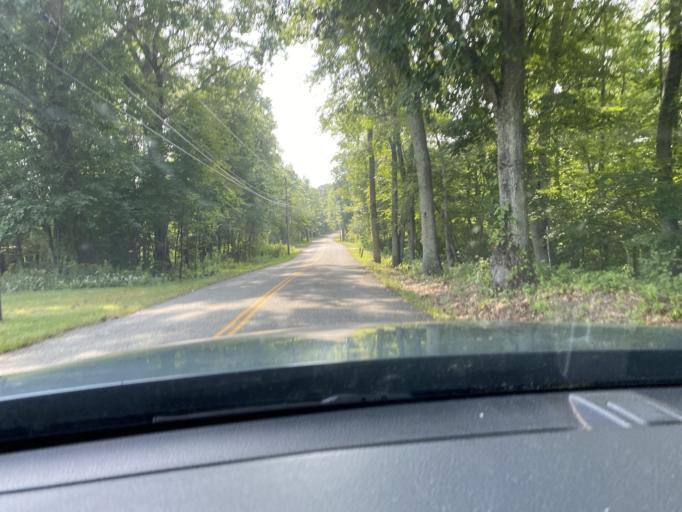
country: US
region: Connecticut
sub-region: New London County
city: Colchester
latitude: 41.6254
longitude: -72.3048
